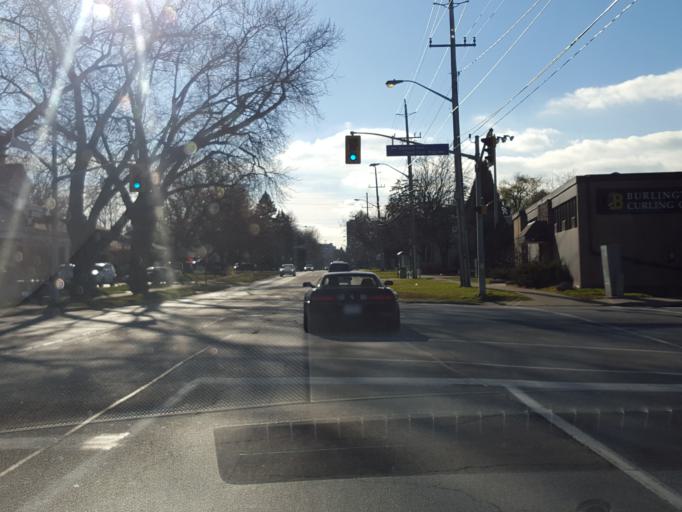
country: CA
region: Ontario
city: Burlington
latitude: 43.3346
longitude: -79.7894
